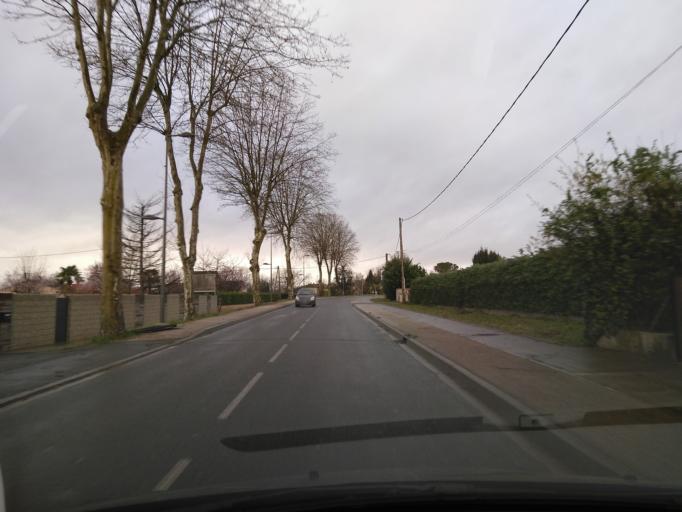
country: FR
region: Midi-Pyrenees
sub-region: Departement de la Haute-Garonne
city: Montesquieu-Volvestre
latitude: 43.2170
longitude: 1.2202
